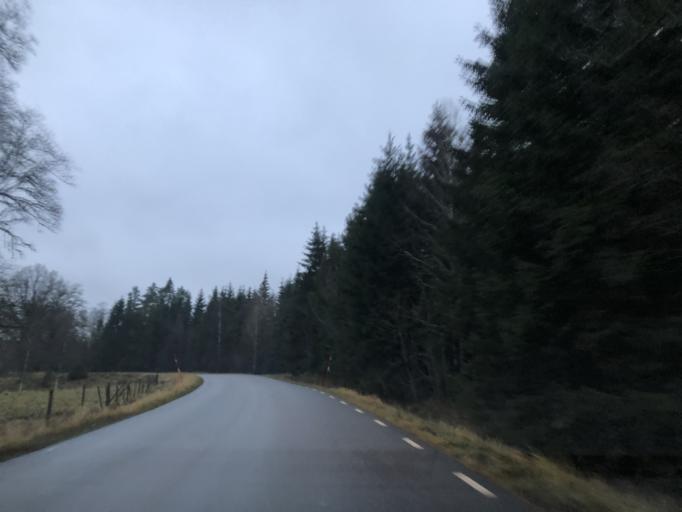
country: SE
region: Vaestra Goetaland
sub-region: Ulricehamns Kommun
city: Ulricehamn
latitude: 57.8478
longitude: 13.2625
